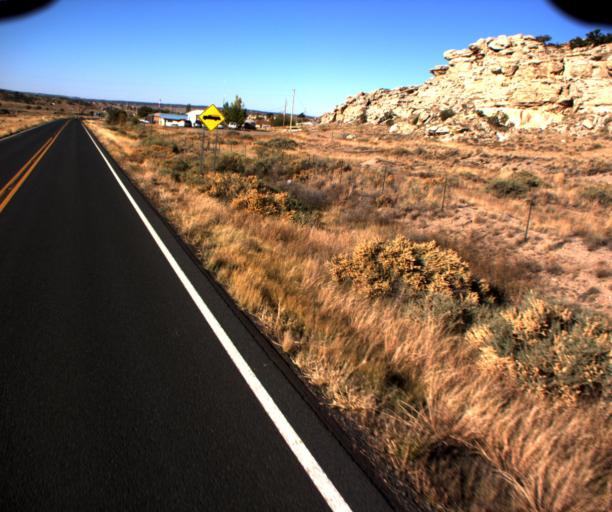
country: US
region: Arizona
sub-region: Apache County
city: Ganado
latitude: 35.7483
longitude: -109.8499
